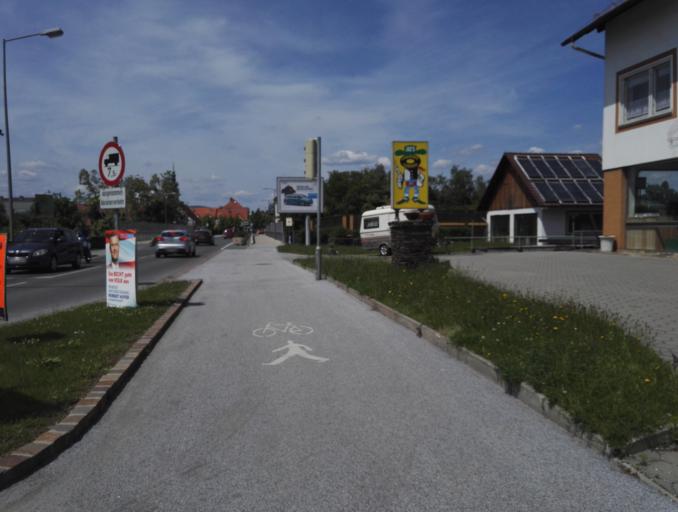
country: AT
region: Styria
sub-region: Politischer Bezirk Graz-Umgebung
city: Feldkirchen bei Graz
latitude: 47.0098
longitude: 15.4448
